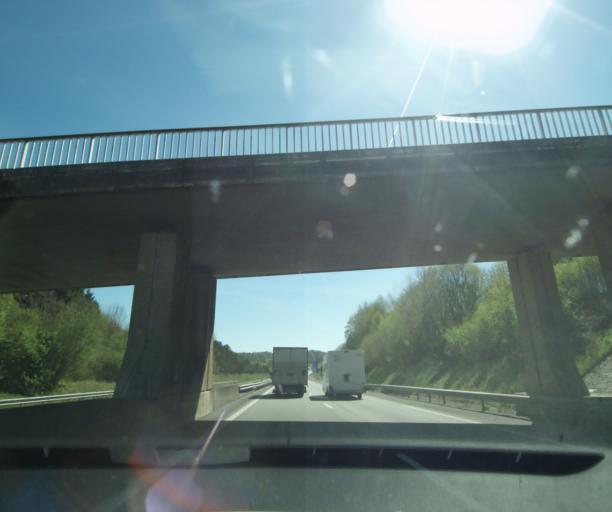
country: FR
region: Limousin
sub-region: Departement de la Correze
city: Vigeois
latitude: 45.3430
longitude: 1.5715
